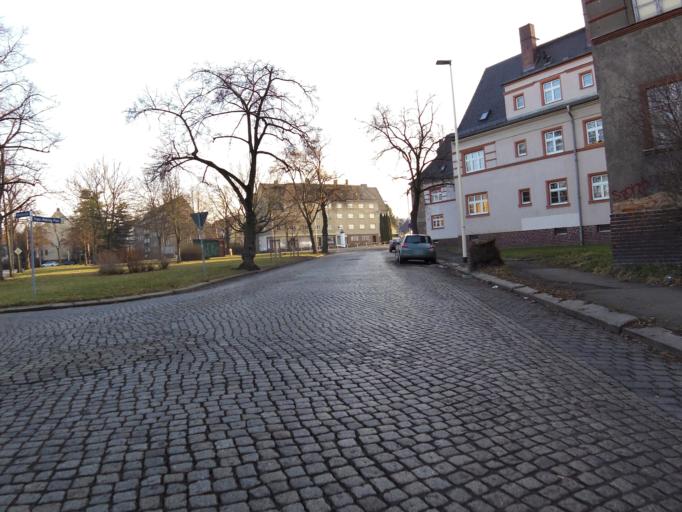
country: DE
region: Saxony
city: Glauchau
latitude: 50.8274
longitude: 12.5527
